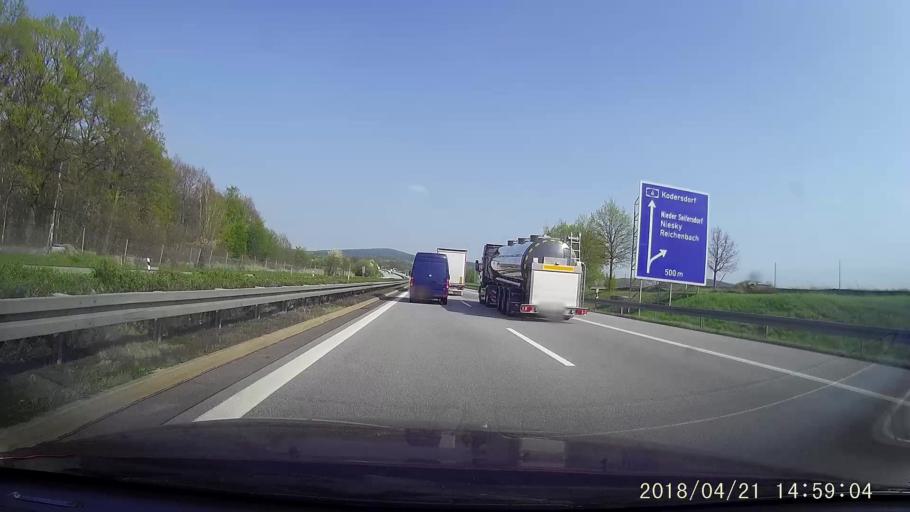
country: DE
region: Saxony
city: Quitzdorf
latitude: 51.2044
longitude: 14.7499
